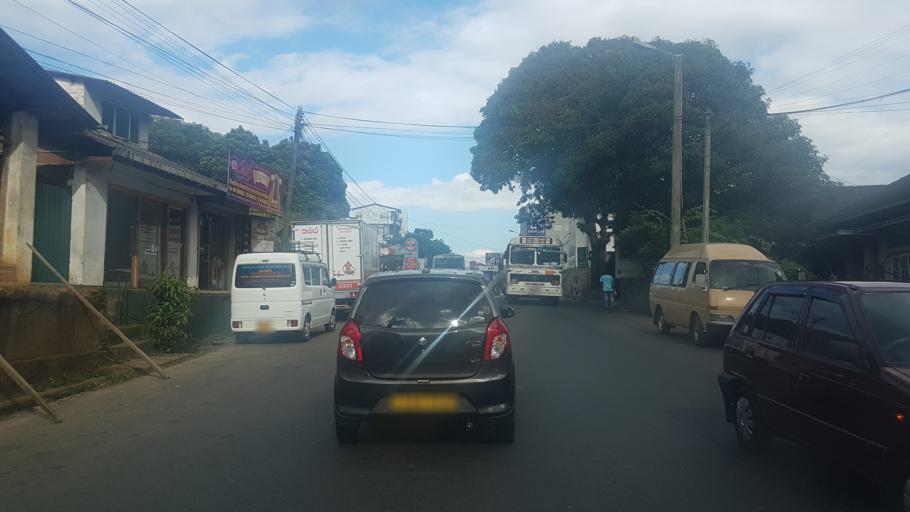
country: LK
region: Central
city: Kandy
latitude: 7.2736
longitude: 80.6091
